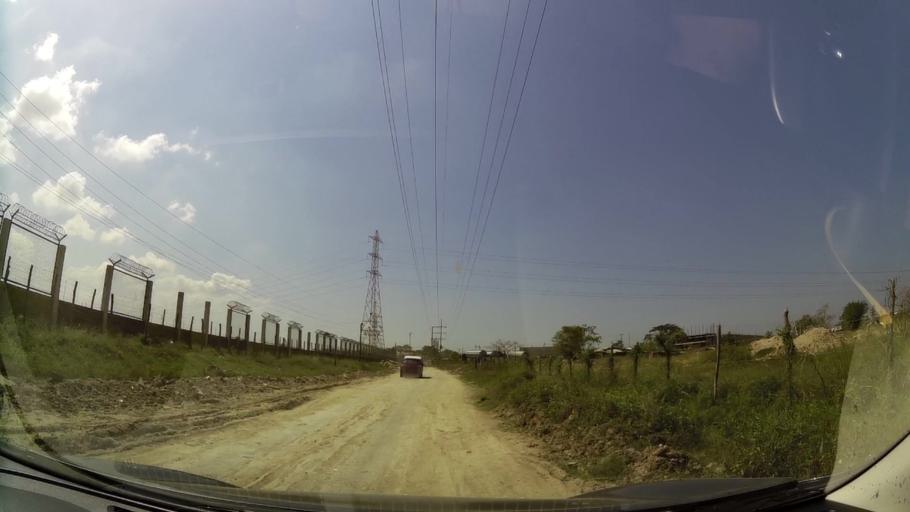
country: CO
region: Bolivar
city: Cartagena
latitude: 10.3502
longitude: -75.4874
